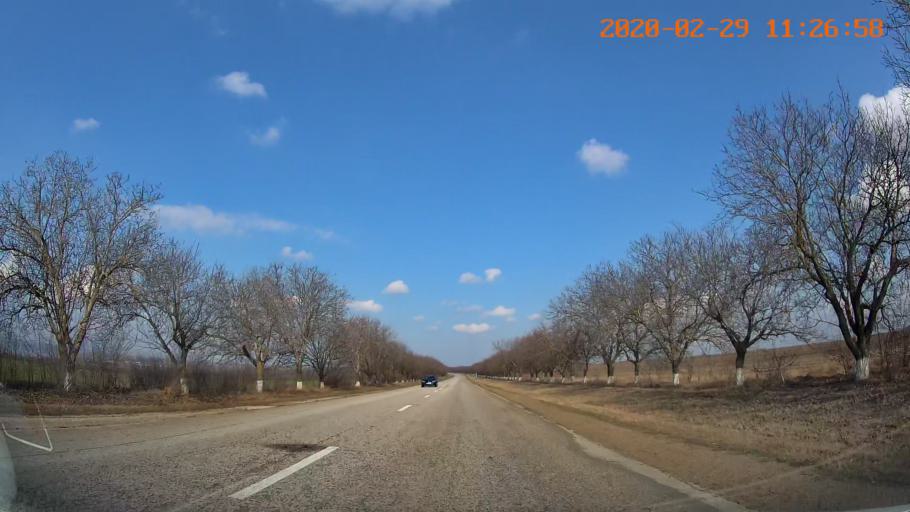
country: MD
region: Telenesti
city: Cocieri
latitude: 47.4610
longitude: 29.1440
